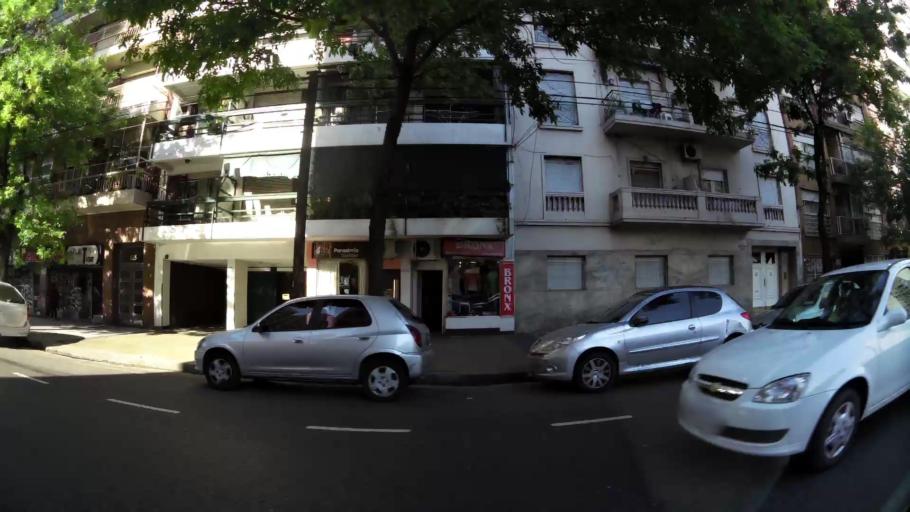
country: AR
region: Buenos Aires F.D.
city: Colegiales
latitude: -34.6117
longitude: -58.4390
